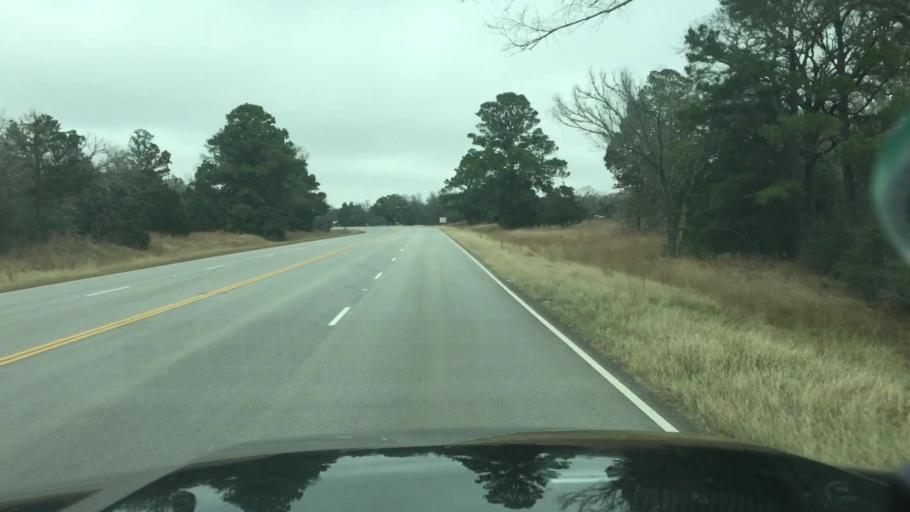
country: US
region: Texas
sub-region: Lee County
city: Giddings
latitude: 30.0908
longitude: -96.9137
